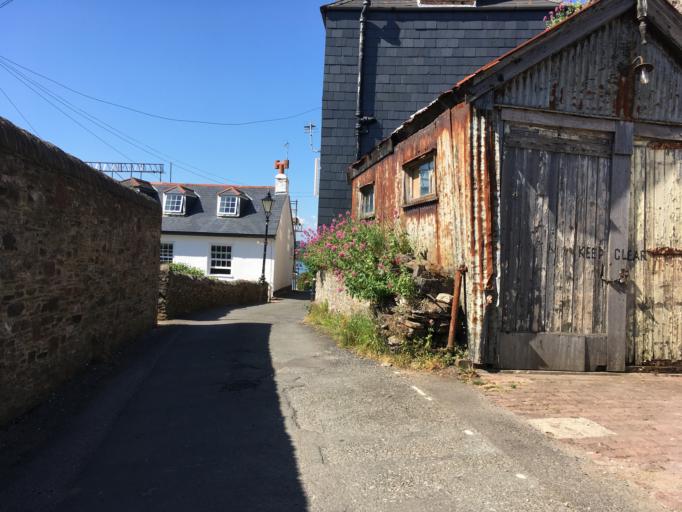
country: GB
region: England
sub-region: Devon
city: Dartmouth
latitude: 50.3479
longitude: -3.5725
